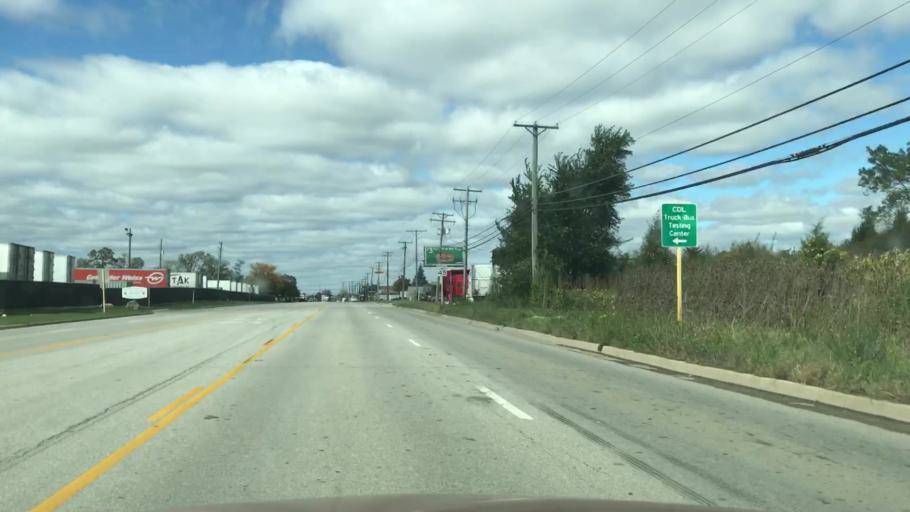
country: US
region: Illinois
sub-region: Cook County
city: Elk Grove Village
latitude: 42.0177
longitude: -87.9528
